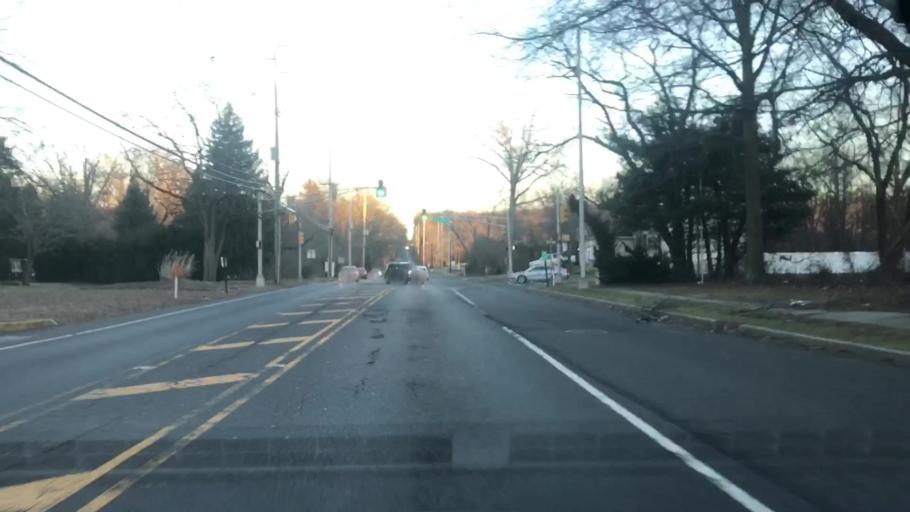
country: US
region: New Jersey
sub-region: Burlington County
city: Burlington
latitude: 40.0498
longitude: -74.8654
